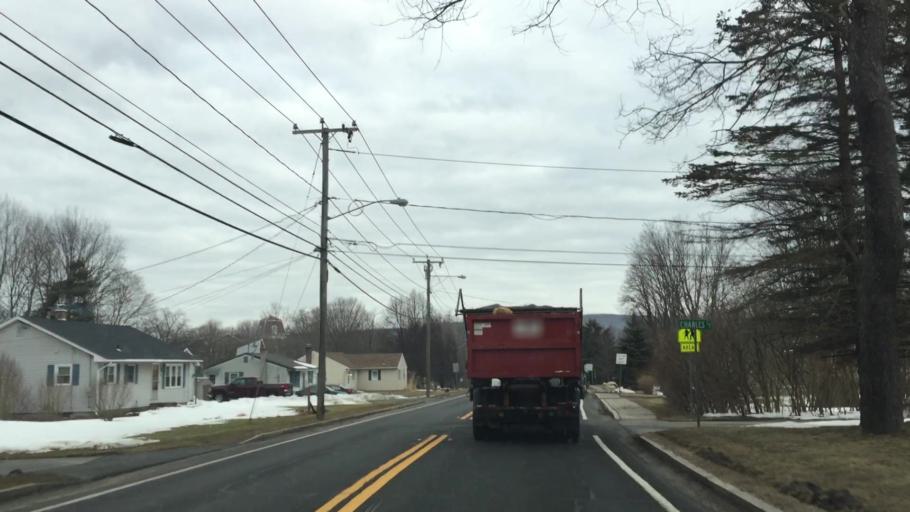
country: US
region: Massachusetts
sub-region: Berkshire County
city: Dalton
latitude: 42.4654
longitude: -73.1391
